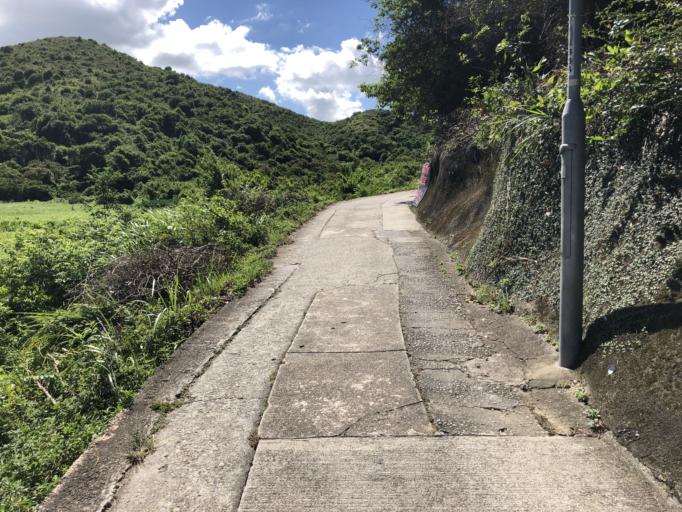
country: HK
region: Tuen Mun
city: Tuen Mun
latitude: 22.2920
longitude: 113.9769
